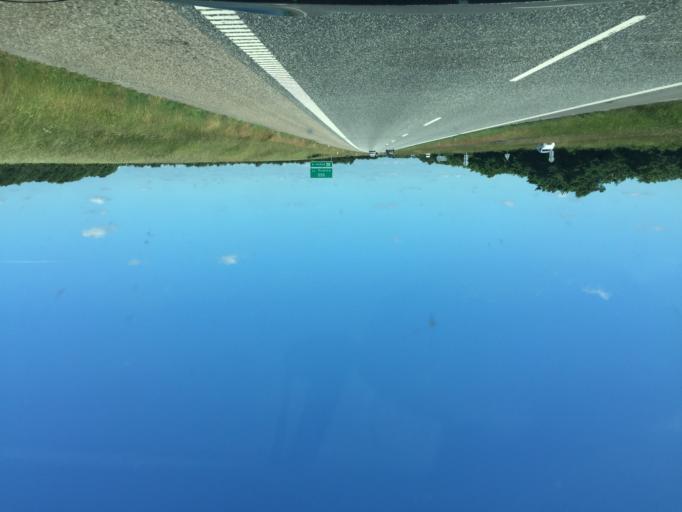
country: DK
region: South Denmark
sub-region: Aabenraa Kommune
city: Krusa
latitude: 54.8829
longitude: 9.3788
